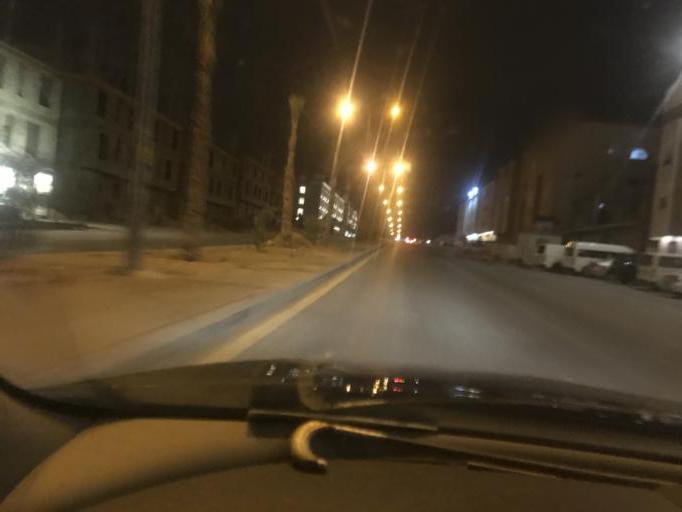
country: SA
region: Ar Riyad
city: Riyadh
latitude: 24.8023
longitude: 46.6836
